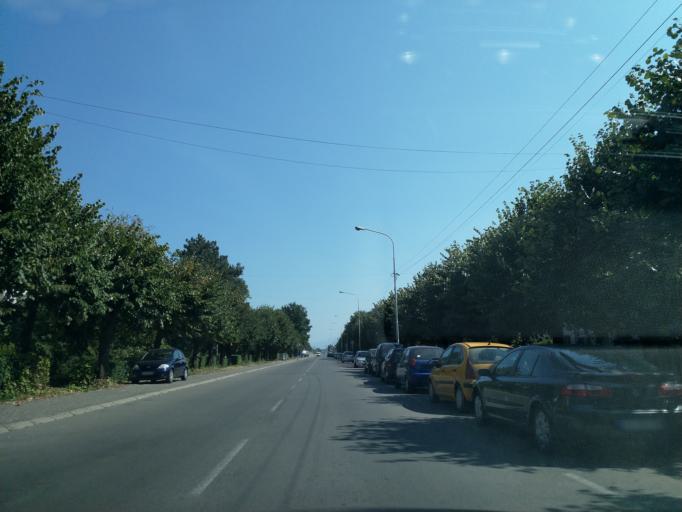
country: RS
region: Central Serbia
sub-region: Rasinski Okrug
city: Trstenik
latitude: 43.6176
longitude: 21.0073
